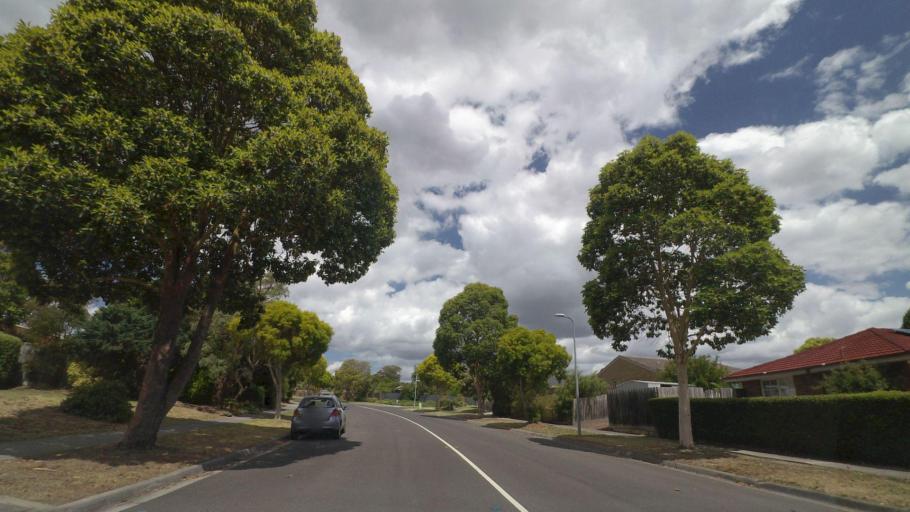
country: AU
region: Victoria
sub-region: Knox
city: Wantirna
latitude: -37.8569
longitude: 145.2189
